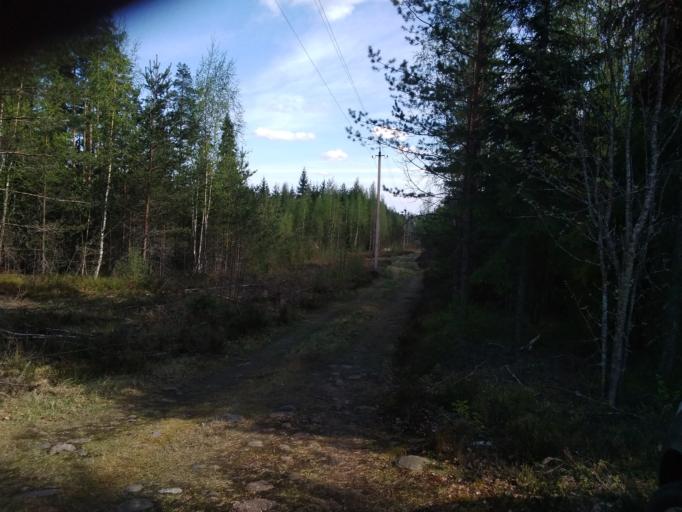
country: RU
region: Leningrad
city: Glebychevo
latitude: 60.3665
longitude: 28.9372
